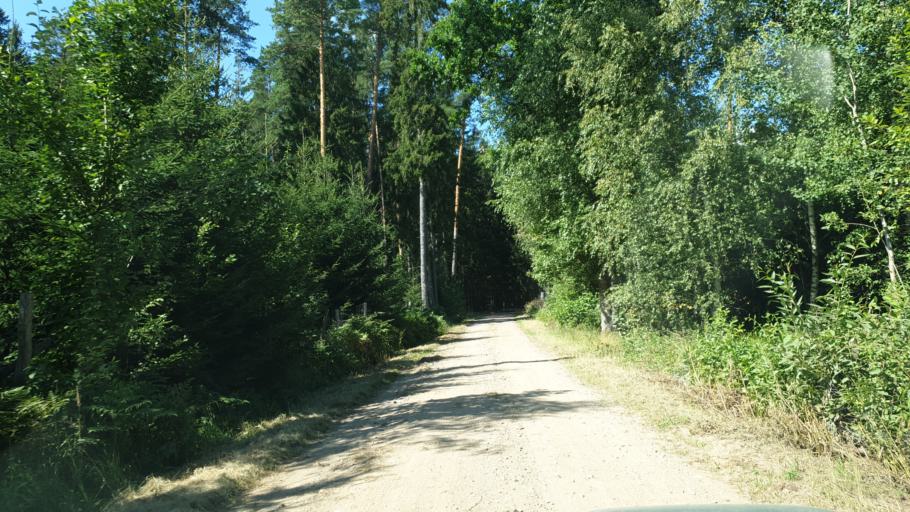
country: LT
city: Sirvintos
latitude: 54.9081
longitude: 24.9405
